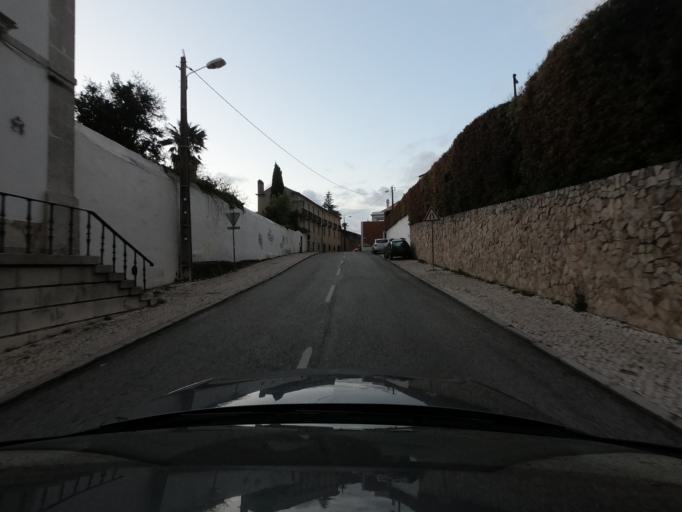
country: PT
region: Lisbon
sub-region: Oeiras
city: Terrugem
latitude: 38.6992
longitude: -9.2727
